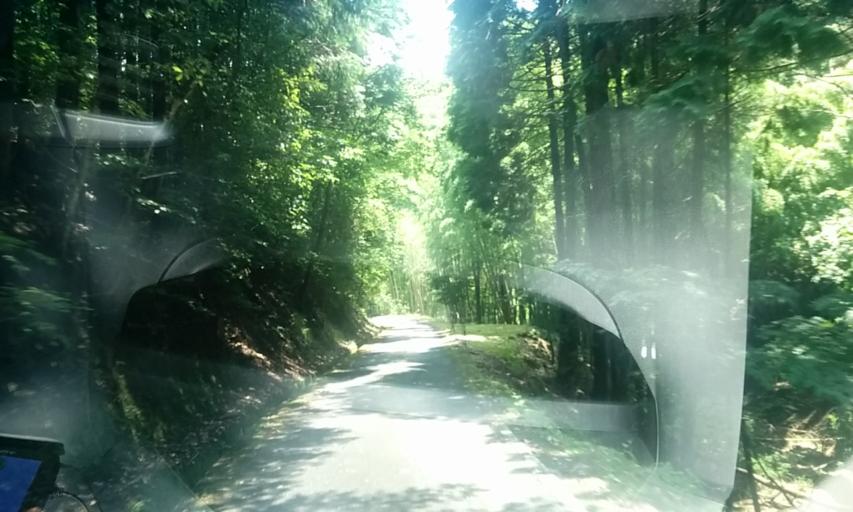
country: JP
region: Hyogo
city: Sasayama
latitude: 35.1740
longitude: 135.2045
